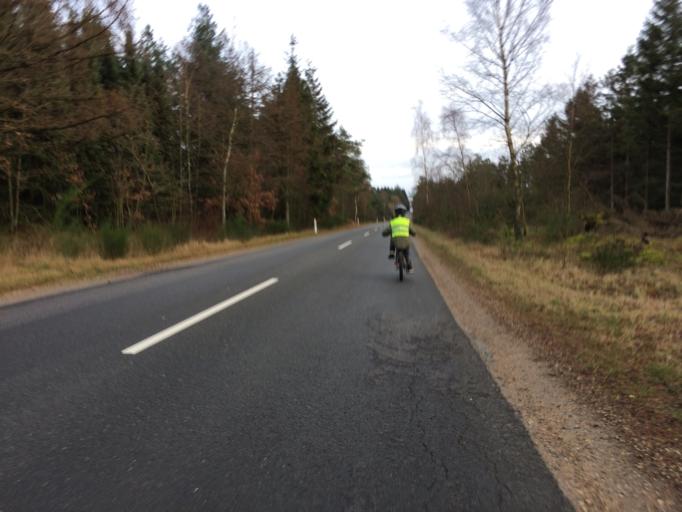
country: DK
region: Central Jutland
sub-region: Holstebro Kommune
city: Ulfborg
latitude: 56.2590
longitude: 8.3496
